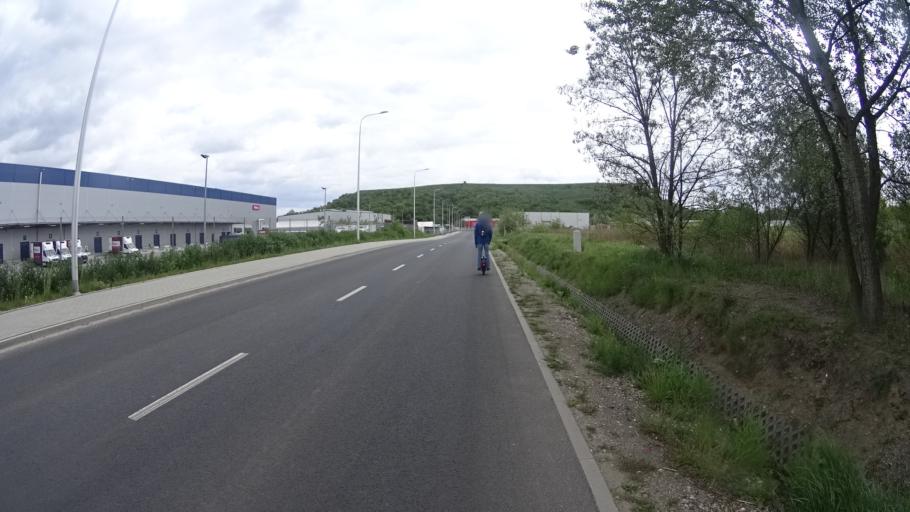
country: PL
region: Masovian Voivodeship
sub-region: Powiat warszawski zachodni
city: Babice
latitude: 52.2774
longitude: 20.8710
